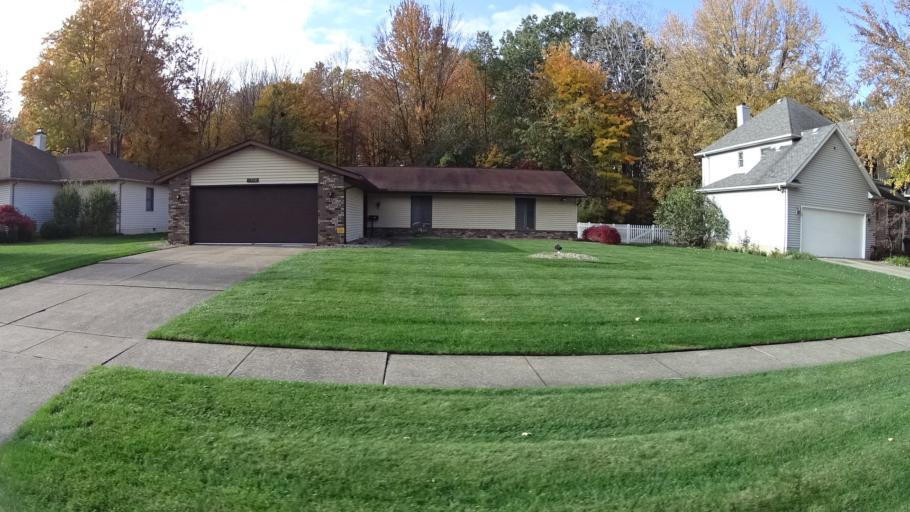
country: US
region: Ohio
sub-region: Lorain County
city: Lorain
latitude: 41.4261
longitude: -82.1819
